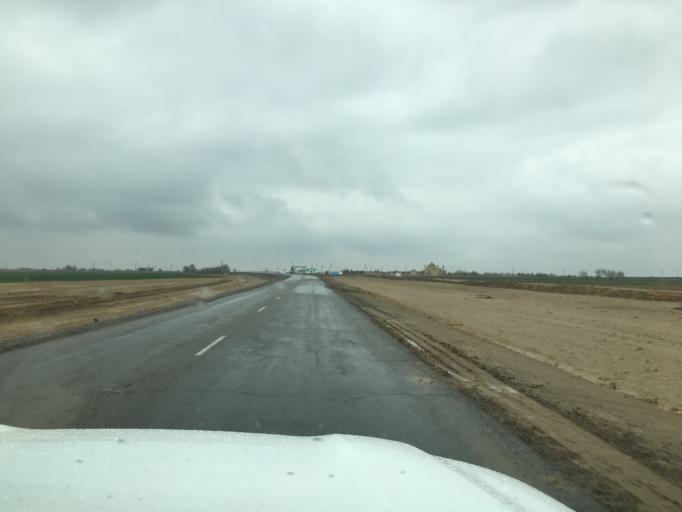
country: TM
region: Mary
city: Bayramaly
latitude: 37.4060
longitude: 62.1723
